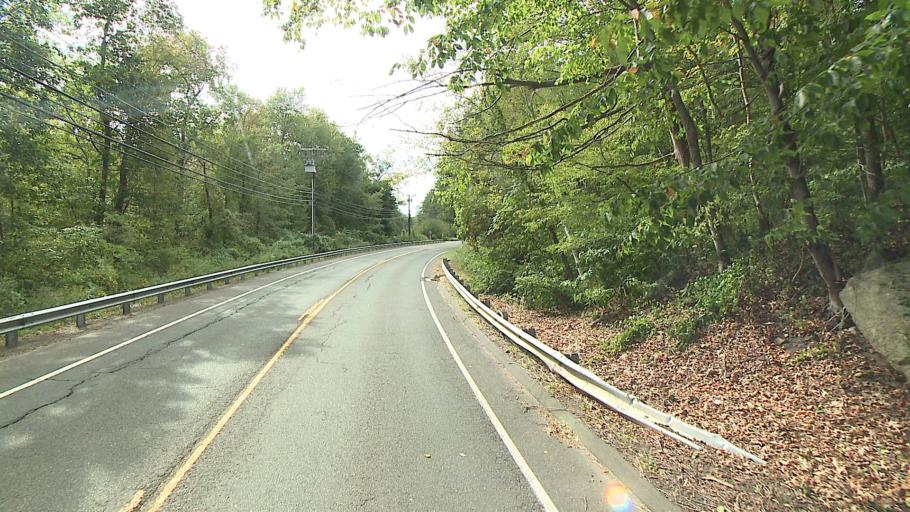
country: US
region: Connecticut
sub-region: Fairfield County
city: New Canaan
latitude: 41.1518
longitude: -73.4779
